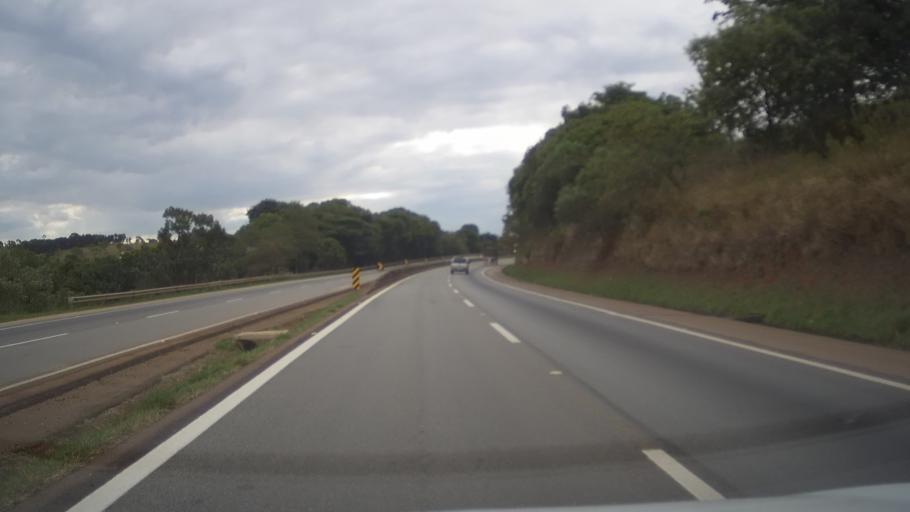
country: BR
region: Minas Gerais
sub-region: Itauna
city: Itauna
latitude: -20.3367
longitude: -44.4448
